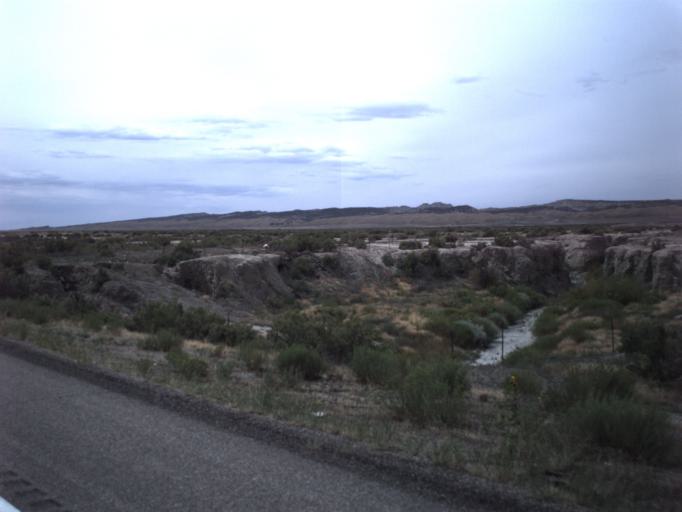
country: US
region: Utah
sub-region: Carbon County
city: East Carbon City
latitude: 39.2404
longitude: -110.3389
